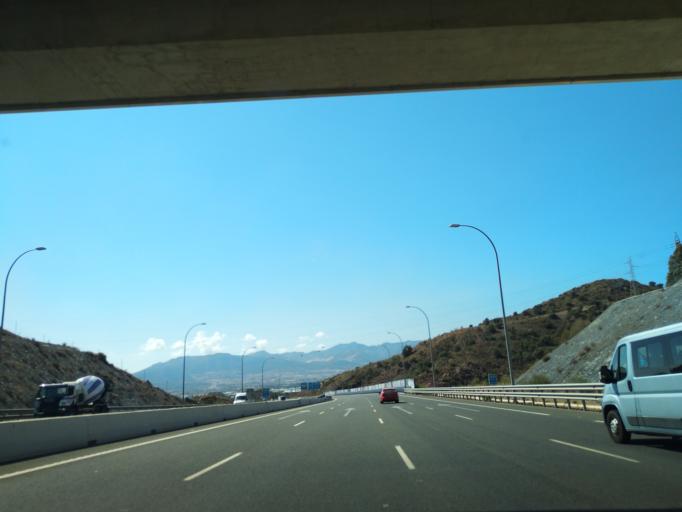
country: ES
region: Andalusia
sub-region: Provincia de Malaga
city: Malaga
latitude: 36.7379
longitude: -4.5048
